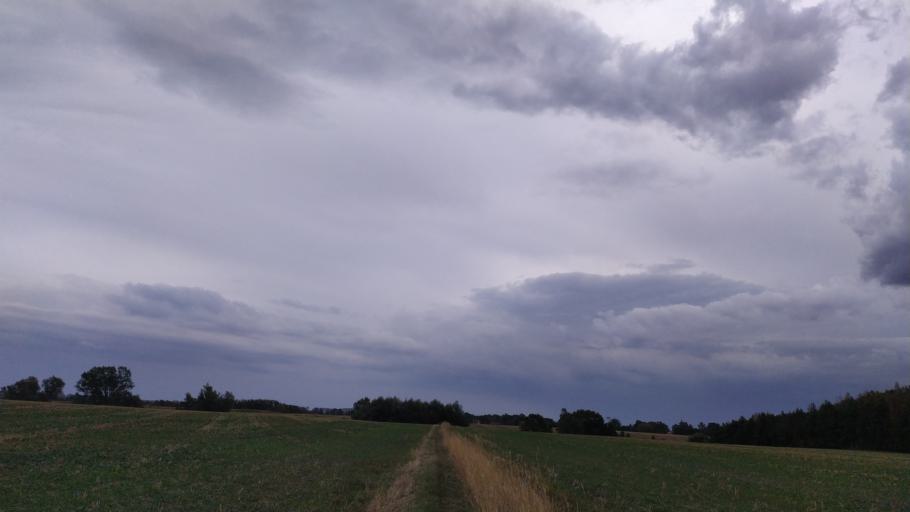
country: DE
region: Mecklenburg-Vorpommern
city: Wolgast
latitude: 54.0467
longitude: 13.8108
